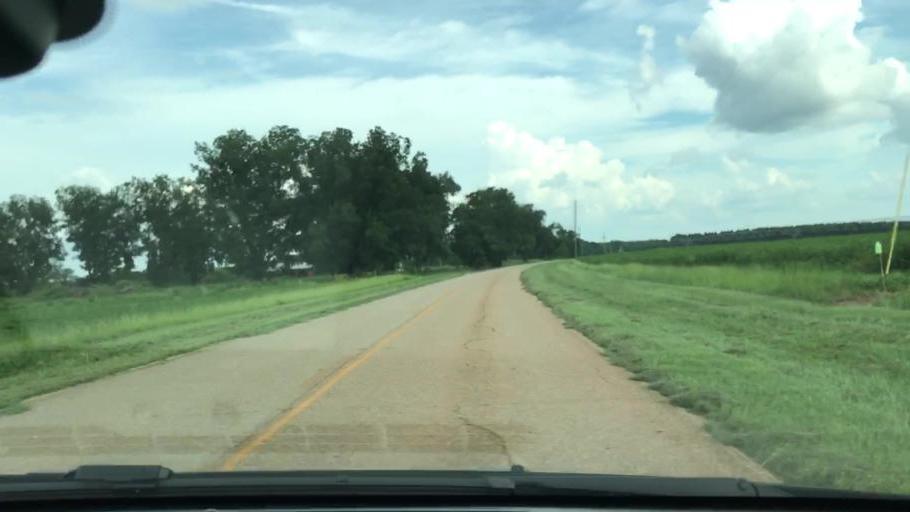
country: US
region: Georgia
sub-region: Clay County
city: Fort Gaines
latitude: 31.5676
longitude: -84.9910
